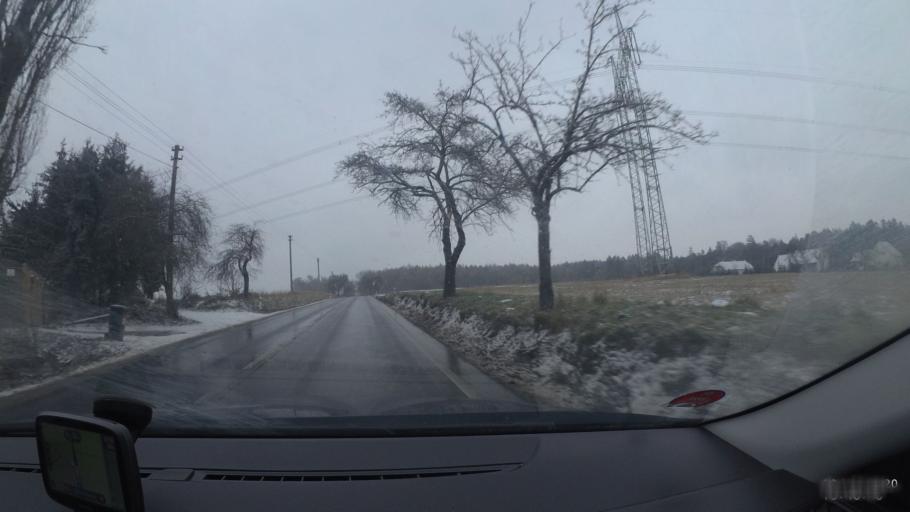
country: CZ
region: Central Bohemia
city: Nove Straseci
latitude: 50.1646
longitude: 13.8986
